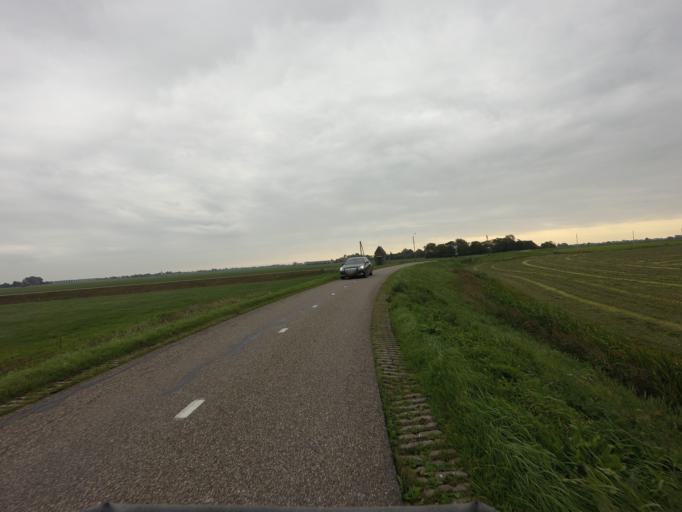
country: NL
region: Friesland
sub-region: Sudwest Fryslan
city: IJlst
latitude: 53.0139
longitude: 5.5719
